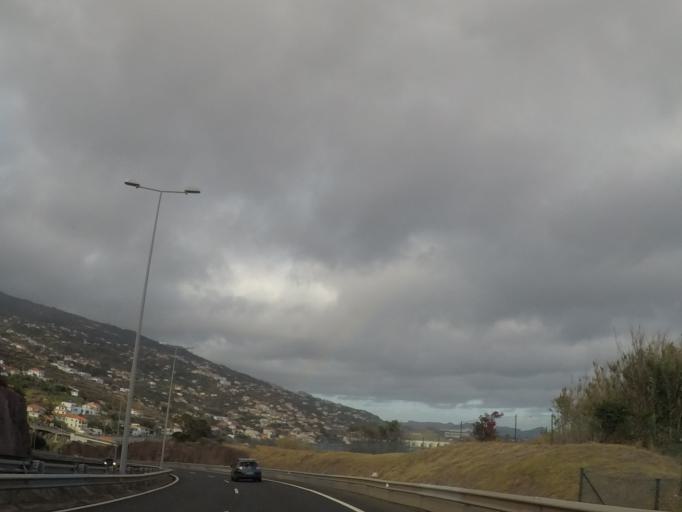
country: PT
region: Madeira
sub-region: Santa Cruz
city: Santa Cruz
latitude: 32.6767
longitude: -16.7992
